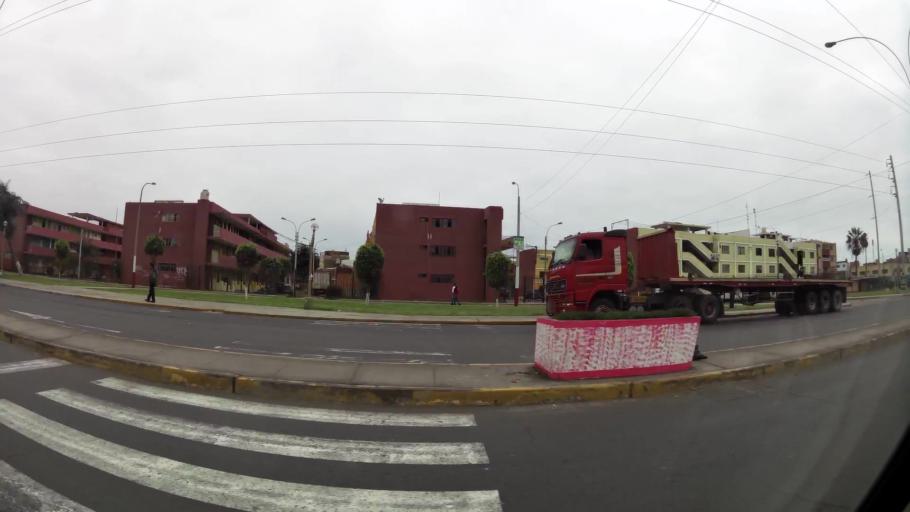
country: PE
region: Callao
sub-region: Callao
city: Callao
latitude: -12.0514
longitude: -77.1330
